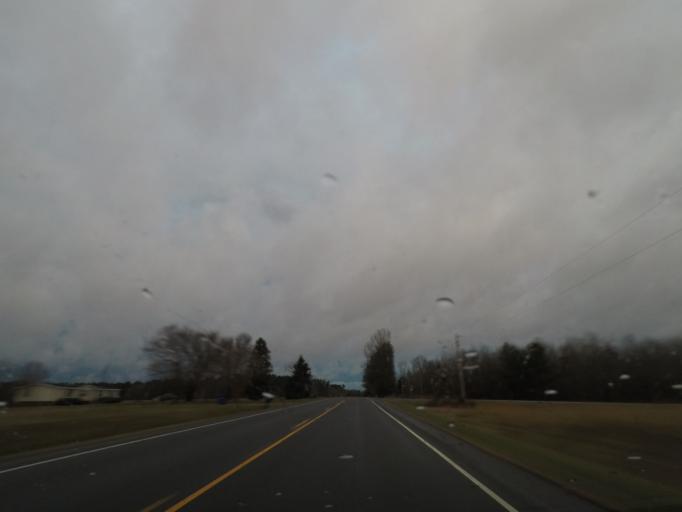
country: US
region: North Carolina
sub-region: Alamance County
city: Mebane
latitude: 36.2214
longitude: -79.1833
